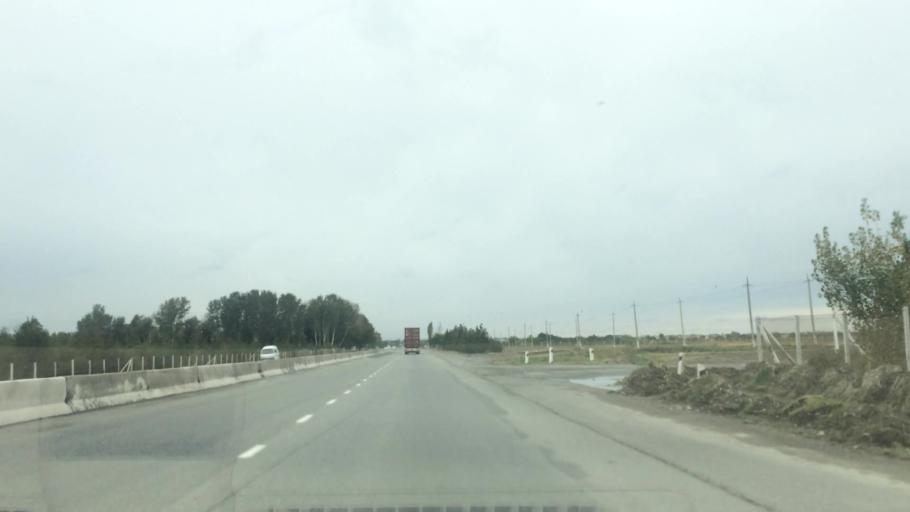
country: UZ
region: Samarqand
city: Bulung'ur
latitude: 39.7811
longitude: 67.2980
